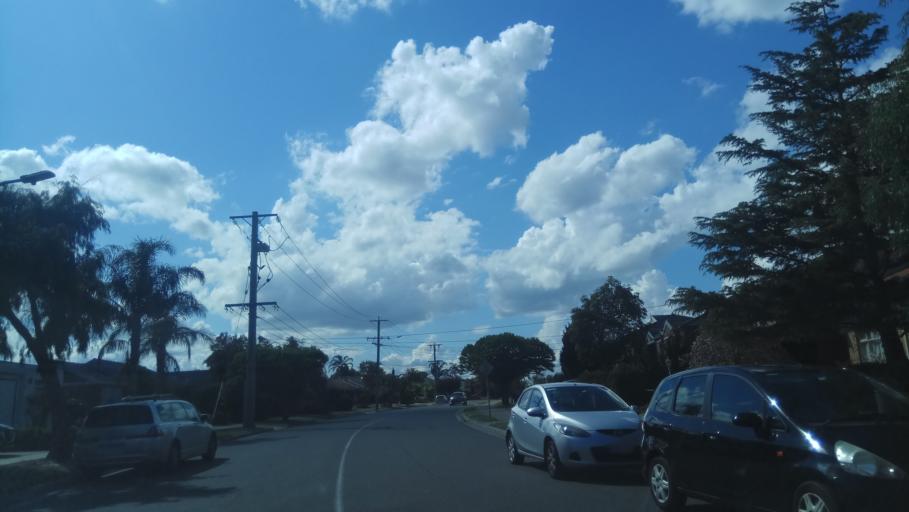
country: AU
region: Victoria
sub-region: Kingston
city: Dingley Village
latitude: -37.9774
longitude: 145.1172
